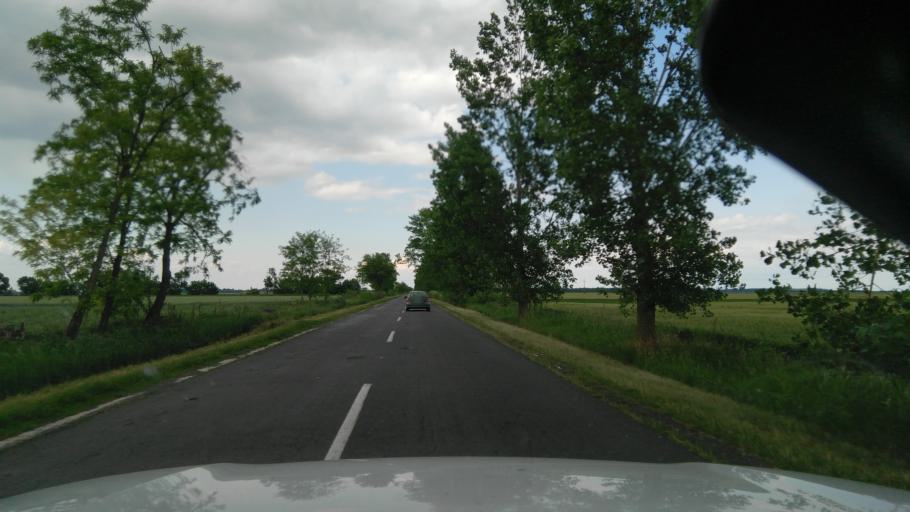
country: HU
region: Bekes
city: Magyarbanhegyes
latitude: 46.4606
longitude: 21.0054
